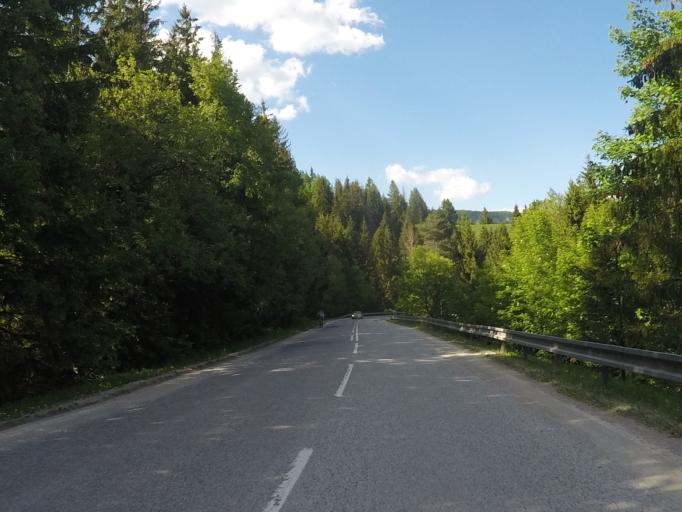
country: SK
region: Kosicky
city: Dobsina
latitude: 48.8508
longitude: 20.3784
